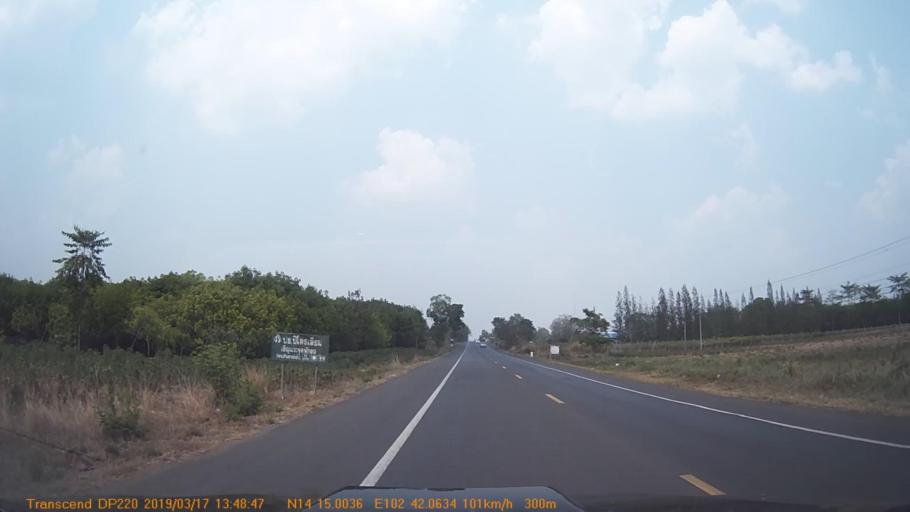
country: TH
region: Buriram
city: Non Din Daeng
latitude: 14.2505
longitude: 102.7013
